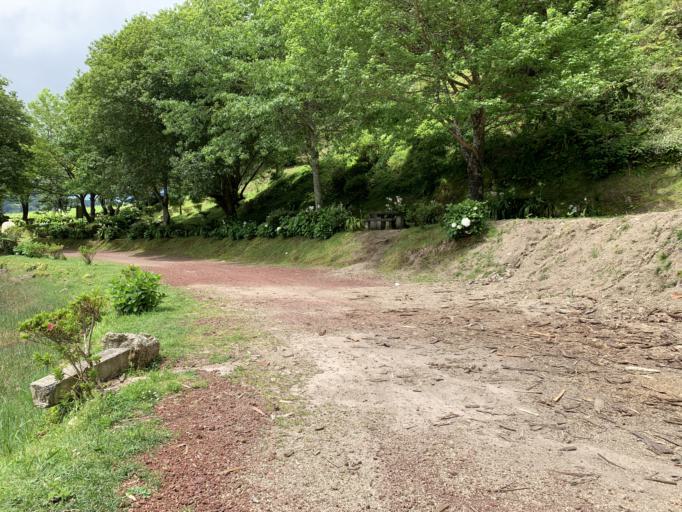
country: PT
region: Azores
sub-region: Ponta Delgada
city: Arrifes
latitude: 37.8487
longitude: -25.7848
